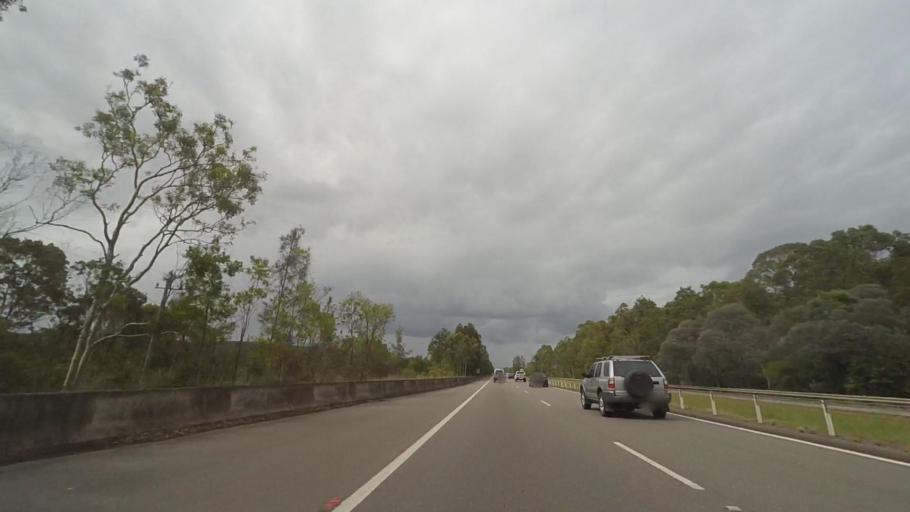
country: AU
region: New South Wales
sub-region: Port Stephens Shire
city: Raymond Terrace
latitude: -32.7357
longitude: 151.7800
